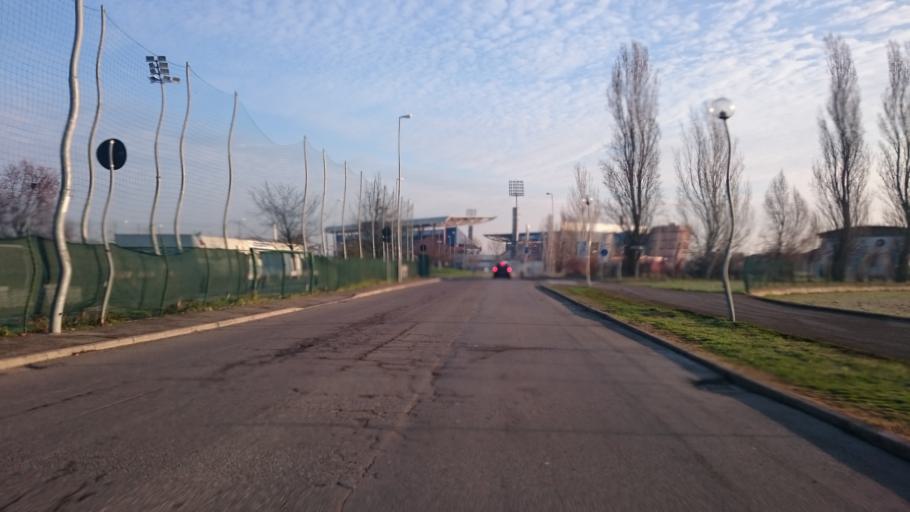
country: IT
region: Emilia-Romagna
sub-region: Provincia di Reggio Emilia
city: Reggio nell'Emilia
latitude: 44.7111
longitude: 10.6473
